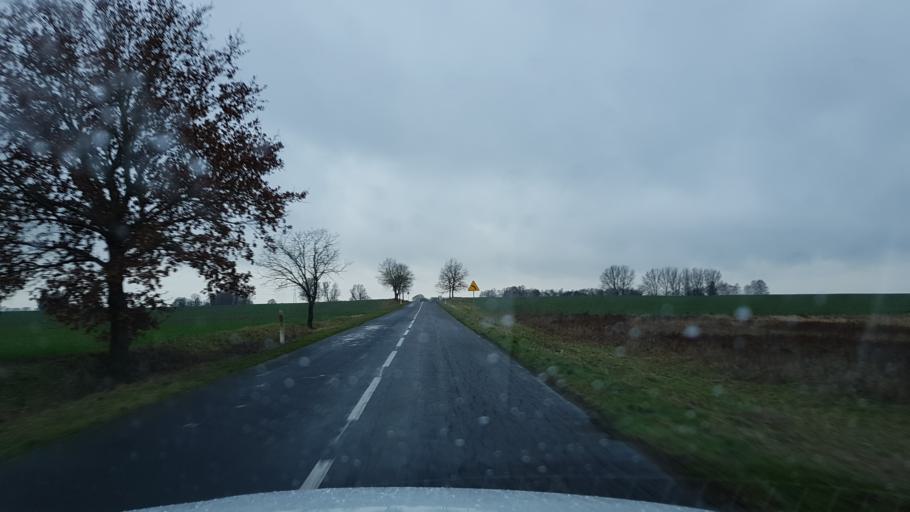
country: PL
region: West Pomeranian Voivodeship
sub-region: Powiat lobeski
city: Radowo Male
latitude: 53.6018
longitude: 15.4286
